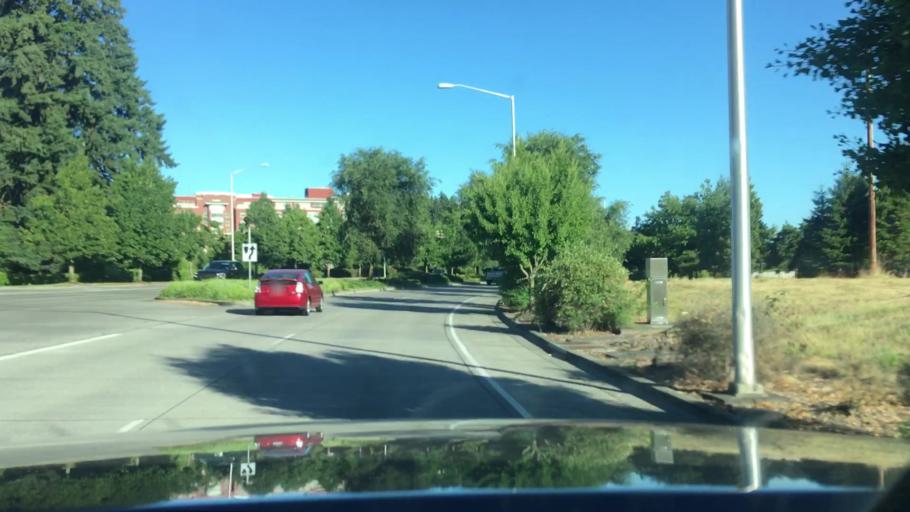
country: US
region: Oregon
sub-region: Lane County
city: Springfield
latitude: 44.0835
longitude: -123.0317
